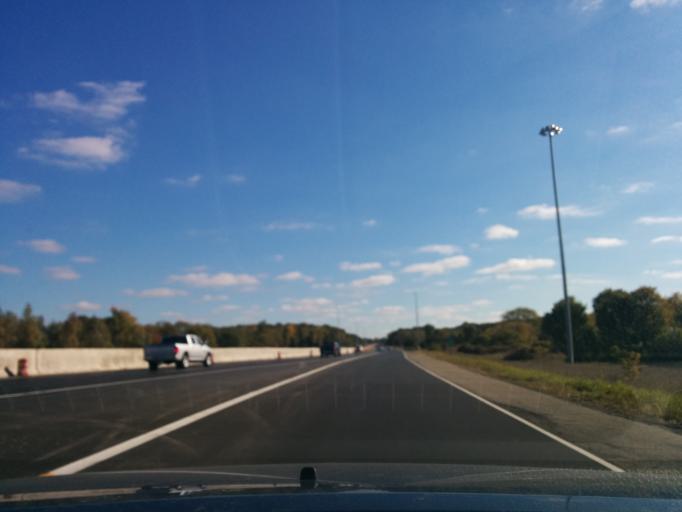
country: US
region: Michigan
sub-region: Oakland County
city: South Lyon
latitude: 42.5171
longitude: -83.6512
